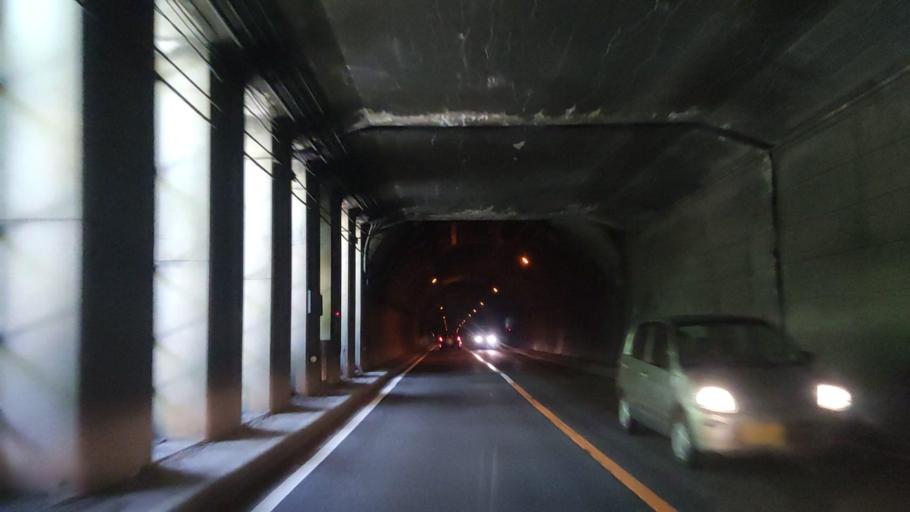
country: JP
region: Niigata
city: Itoigawa
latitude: 36.9230
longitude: 137.8713
